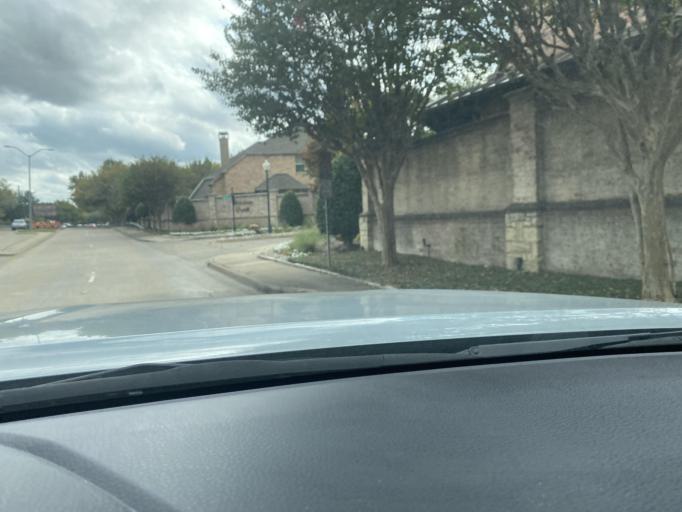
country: US
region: Texas
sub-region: Dallas County
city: Addison
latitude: 33.0002
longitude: -96.7856
